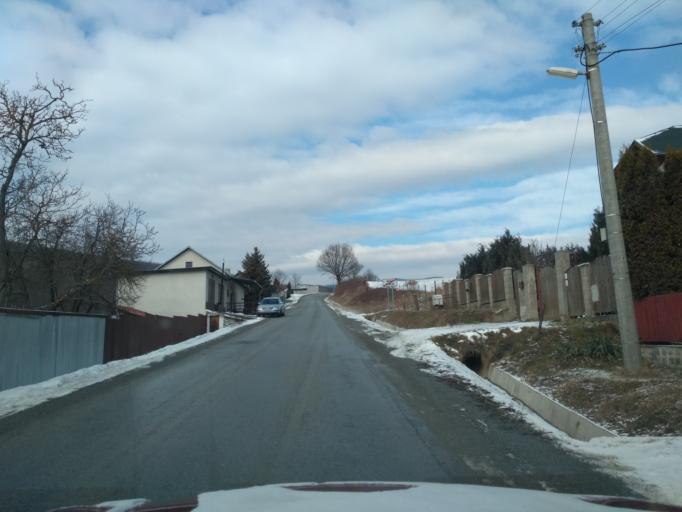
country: SK
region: Kosicky
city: Kosice
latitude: 48.7287
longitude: 21.1375
